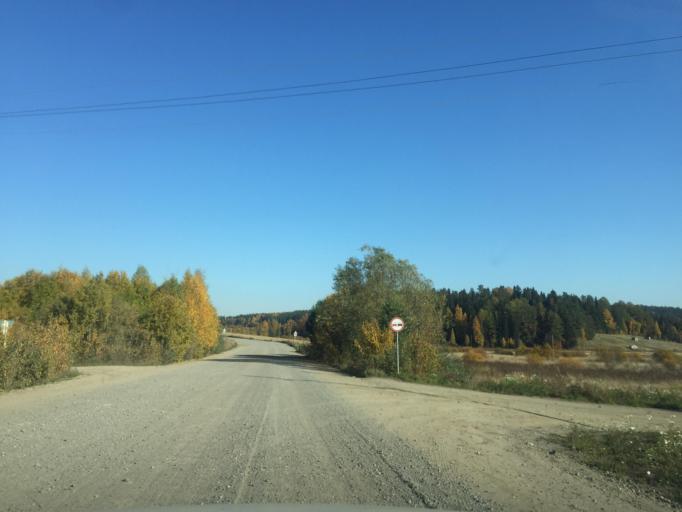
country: RU
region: Leningrad
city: Kuznechnoye
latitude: 61.3054
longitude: 29.9261
